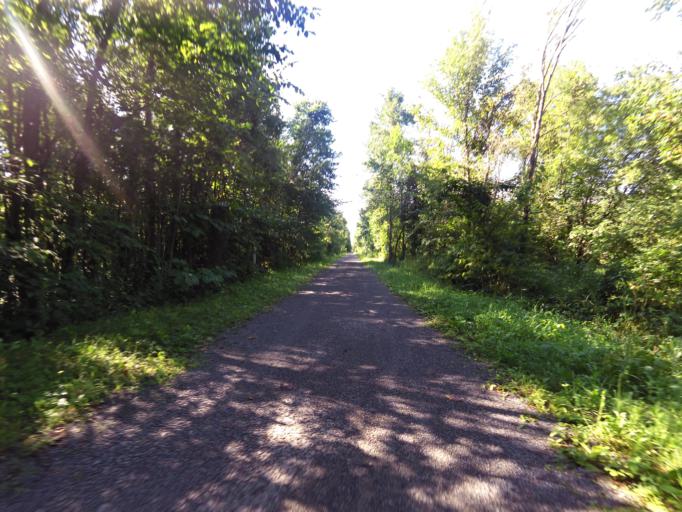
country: CA
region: Ontario
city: Ottawa
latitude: 45.2464
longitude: -75.6207
